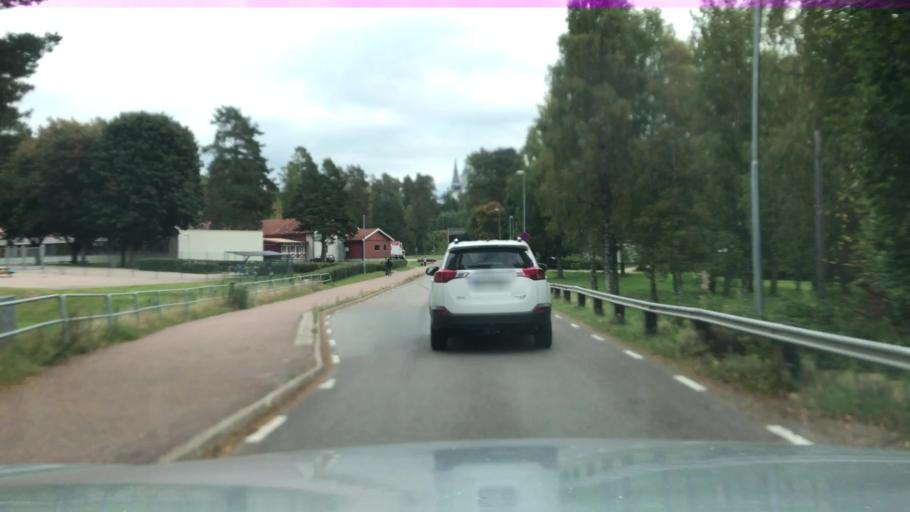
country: SE
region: Vaermland
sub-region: Munkfors Kommun
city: Munkfors
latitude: 59.8363
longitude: 13.5303
